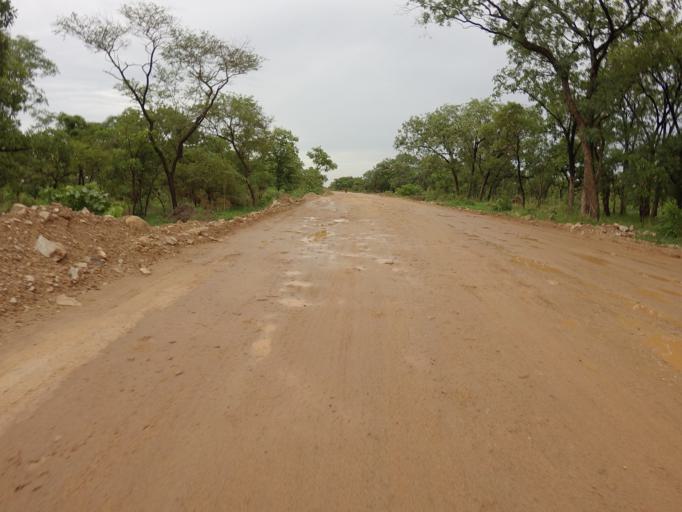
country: GH
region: Upper East
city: Bolgatanga
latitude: 10.8783
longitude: -0.6351
